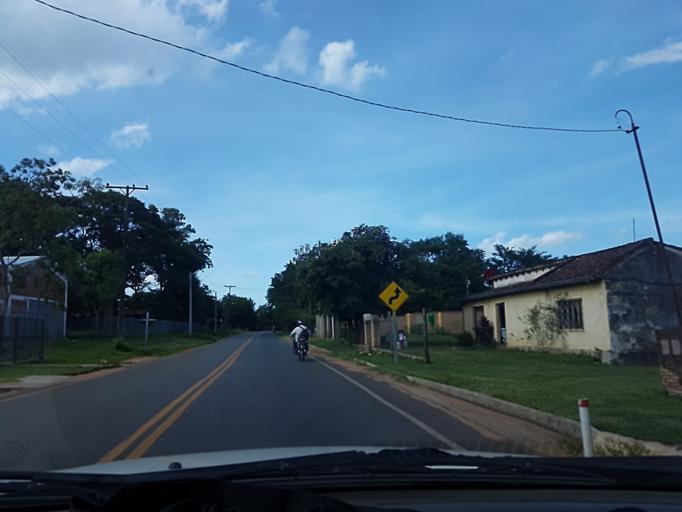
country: PY
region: Central
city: Limpio
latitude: -25.2334
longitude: -57.4495
